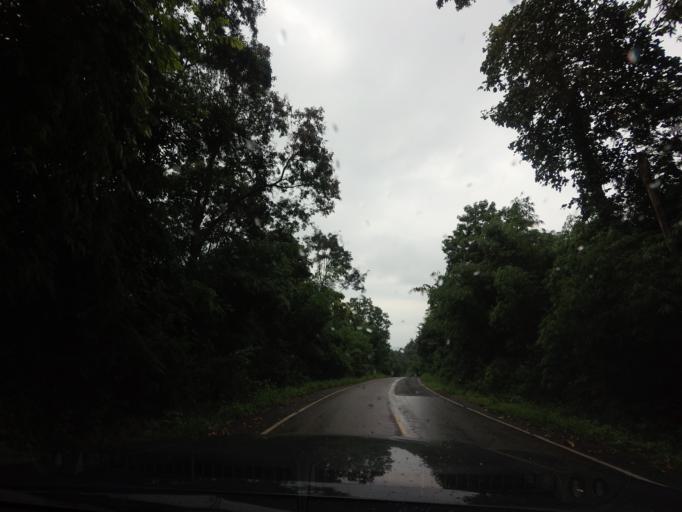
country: TH
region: Nong Khai
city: Sangkhom
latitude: 18.0374
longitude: 102.3162
